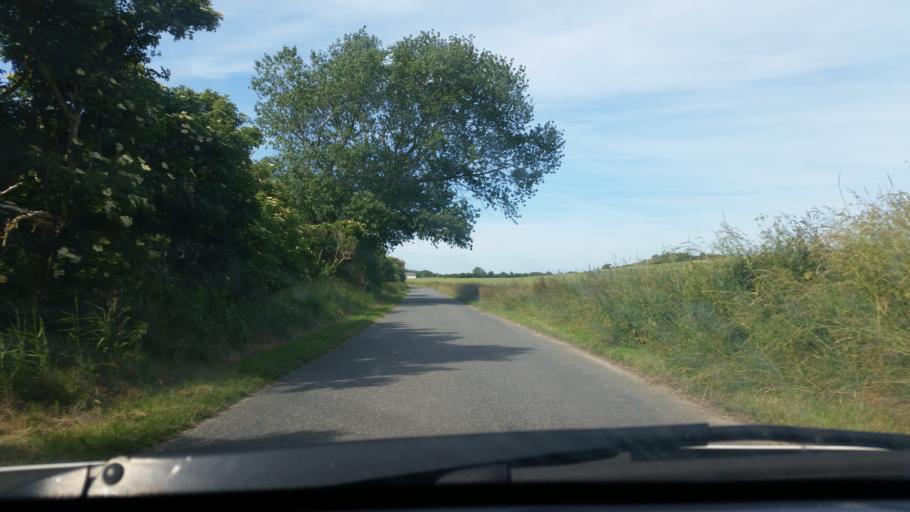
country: DK
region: Central Jutland
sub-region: Samso Kommune
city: Tranebjerg
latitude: 55.7754
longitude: 10.5526
